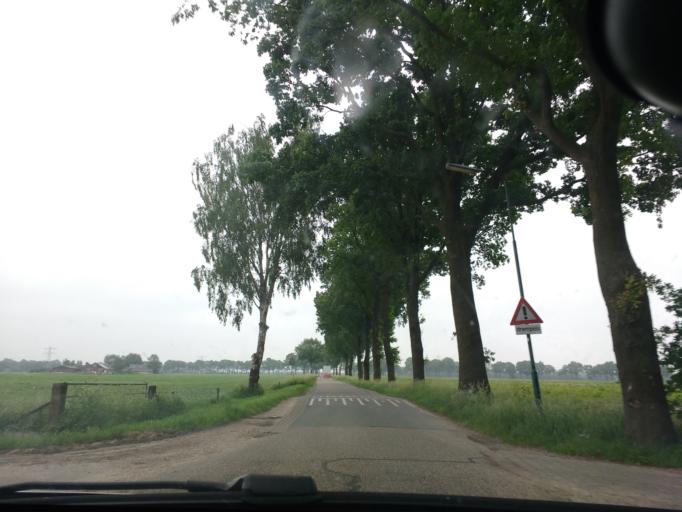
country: NL
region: Utrecht
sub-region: Gemeente Rhenen
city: Rhenen
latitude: 51.9936
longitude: 5.5814
